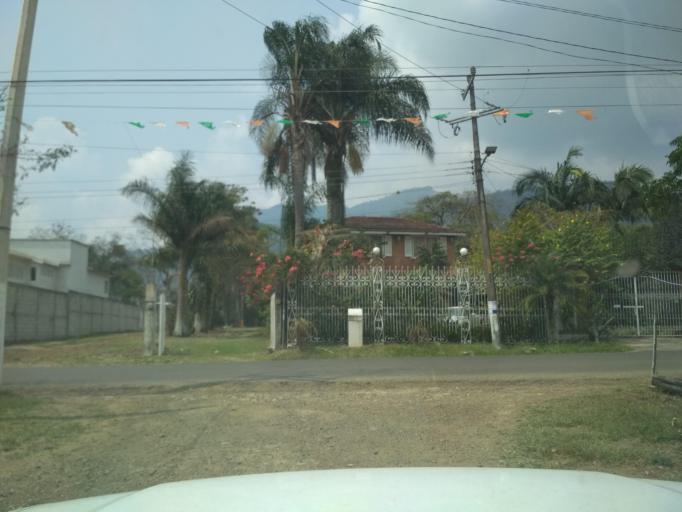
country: MX
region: Veracruz
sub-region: Cordoba
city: Fredepo
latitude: 18.8593
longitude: -96.9833
